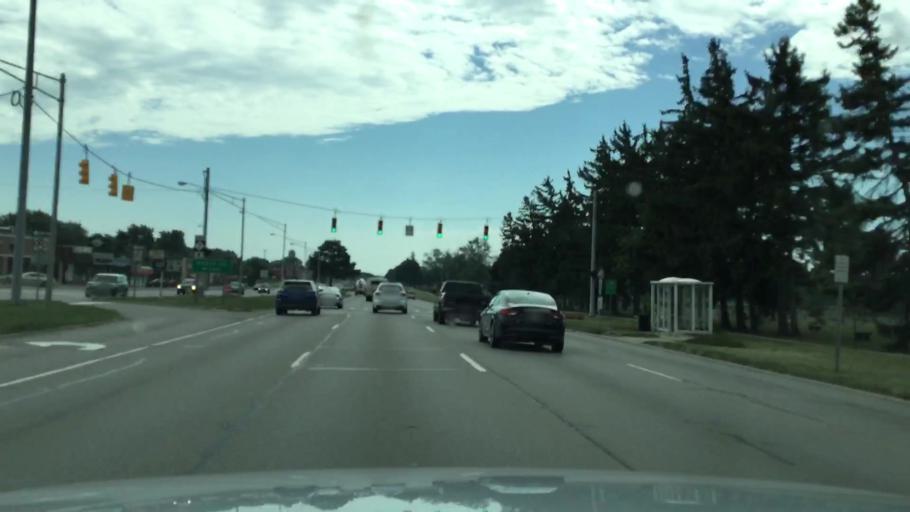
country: US
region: Michigan
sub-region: Oakland County
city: Berkley
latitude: 42.5109
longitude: -83.1796
